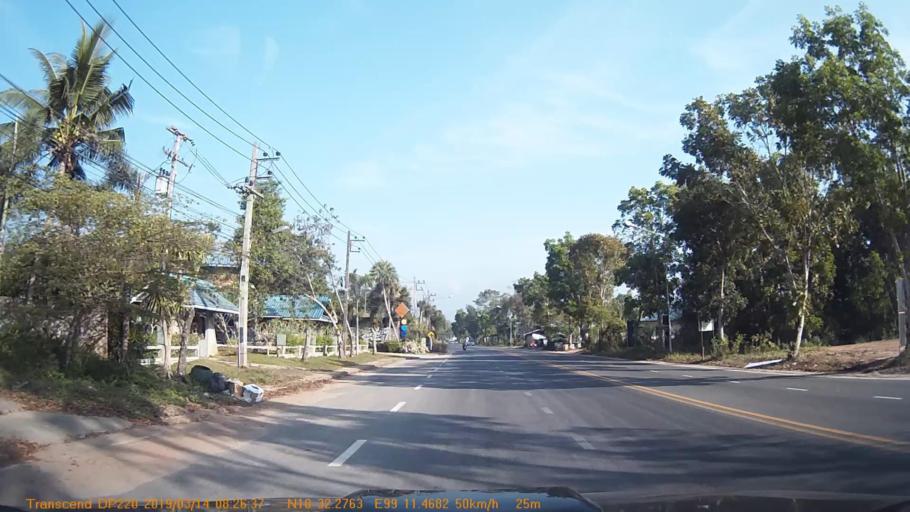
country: TH
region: Chumphon
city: Chumphon
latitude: 10.5381
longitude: 99.1911
